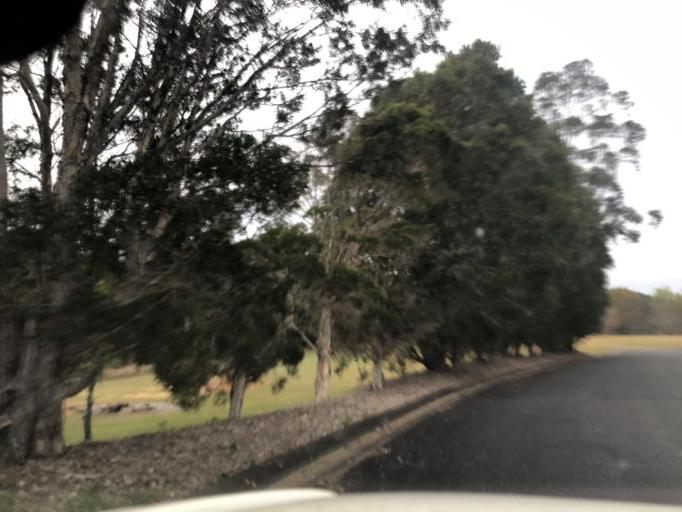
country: AU
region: New South Wales
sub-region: Coffs Harbour
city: Coffs Harbour
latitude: -30.2543
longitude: 153.0536
